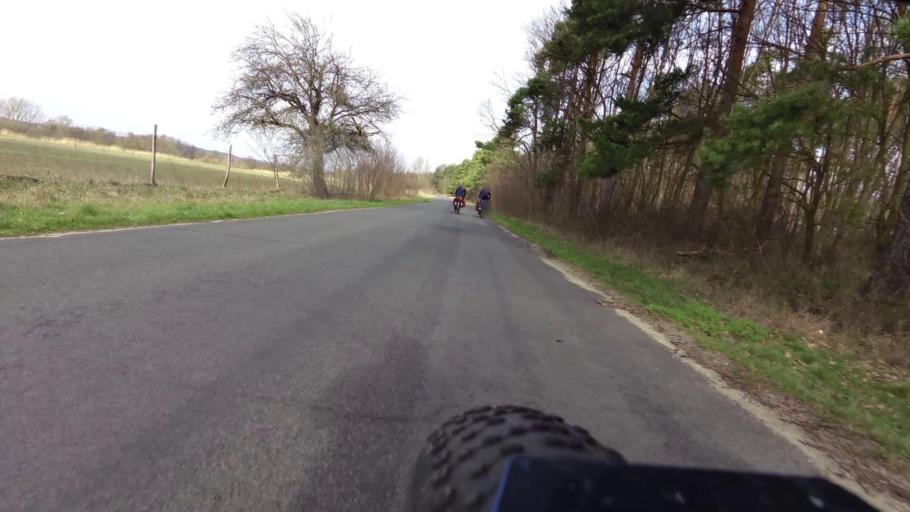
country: DE
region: Brandenburg
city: Brieskow-Finkenheerd
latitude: 52.2896
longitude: 14.6111
